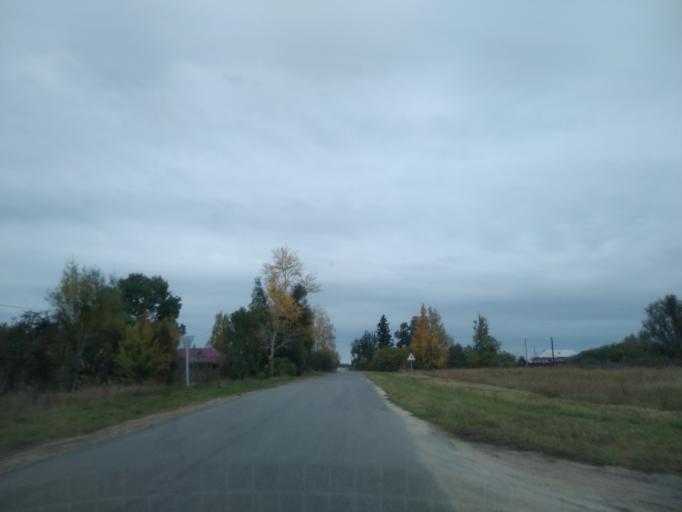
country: RU
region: Lipetsk
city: Zadonsk
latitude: 52.3150
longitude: 38.9200
